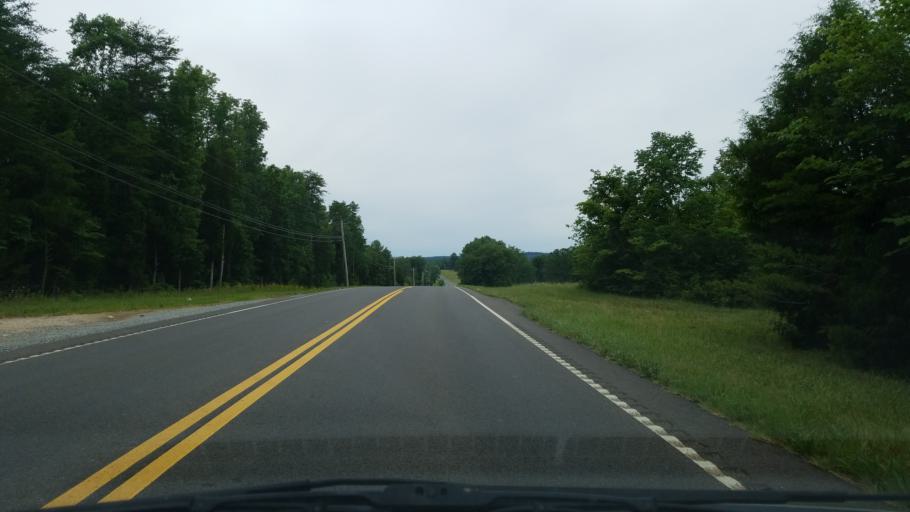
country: US
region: Tennessee
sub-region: Bradley County
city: Hopewell
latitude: 35.3164
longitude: -84.9466
